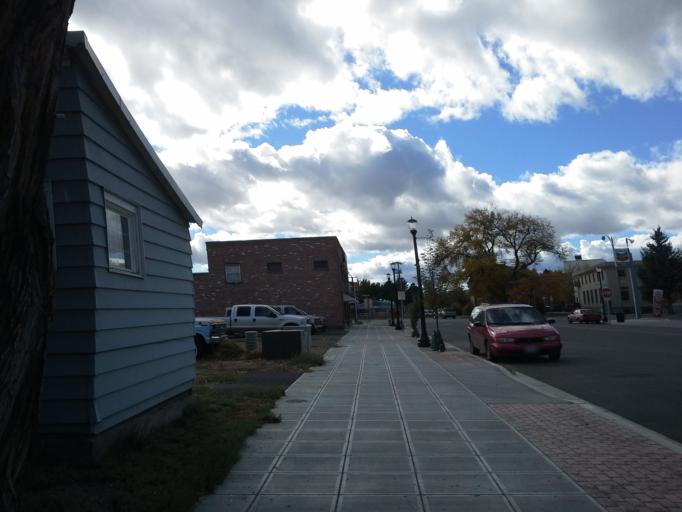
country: US
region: Oregon
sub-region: Baker County
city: Baker City
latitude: 44.7751
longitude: -117.8290
